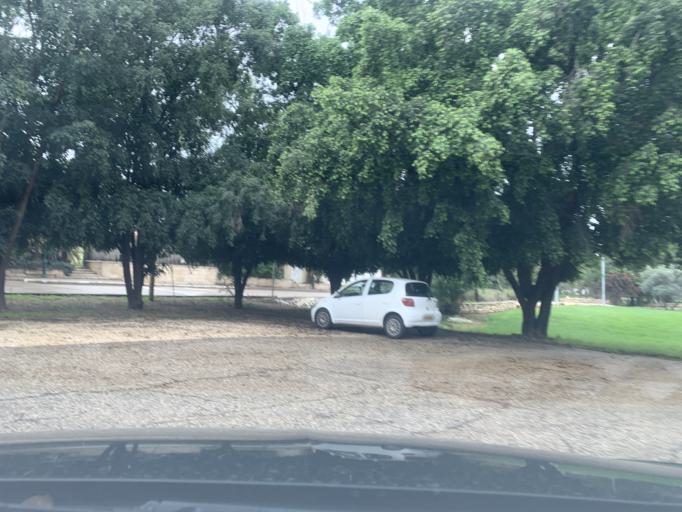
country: PS
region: West Bank
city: Qalqilyah
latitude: 32.2109
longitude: 34.9788
